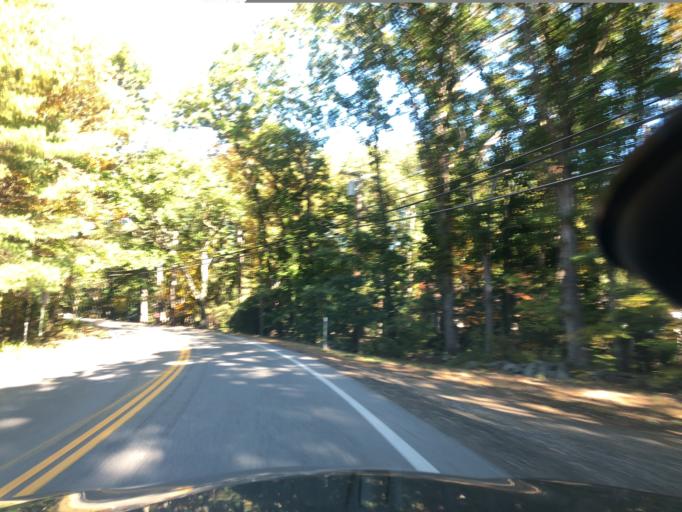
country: US
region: New Hampshire
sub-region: Rockingham County
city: Exeter
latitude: 43.0197
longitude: -70.9403
